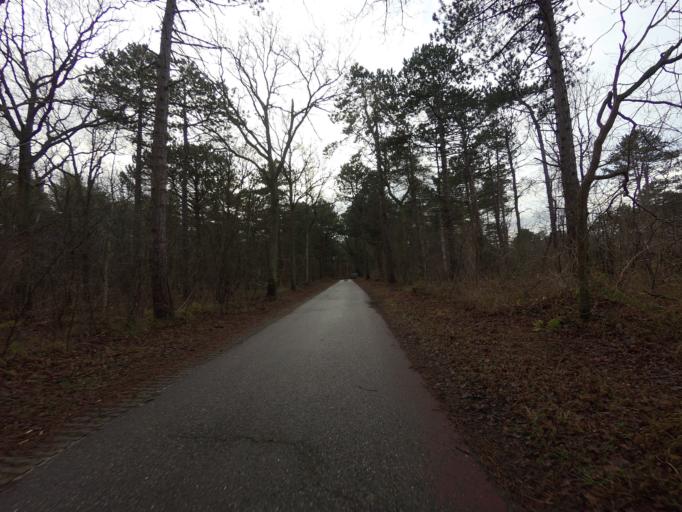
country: NL
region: North Holland
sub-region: Gemeente Texel
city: Den Burg
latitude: 53.0531
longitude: 4.7353
